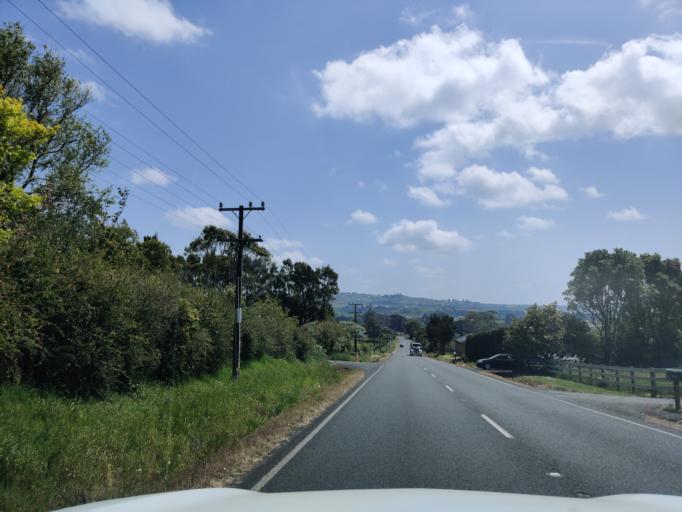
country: NZ
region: Auckland
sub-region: Auckland
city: Pukekohe East
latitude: -37.2136
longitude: 174.9420
